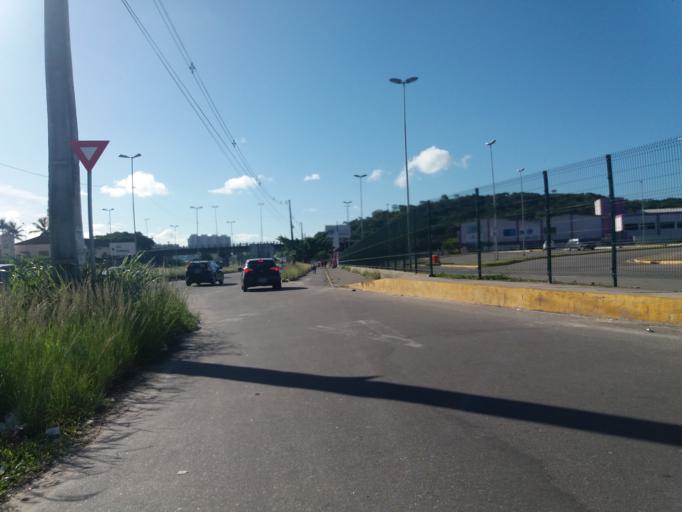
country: BR
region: Pernambuco
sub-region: Paulista
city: Paulista
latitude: -7.9398
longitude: -34.8787
